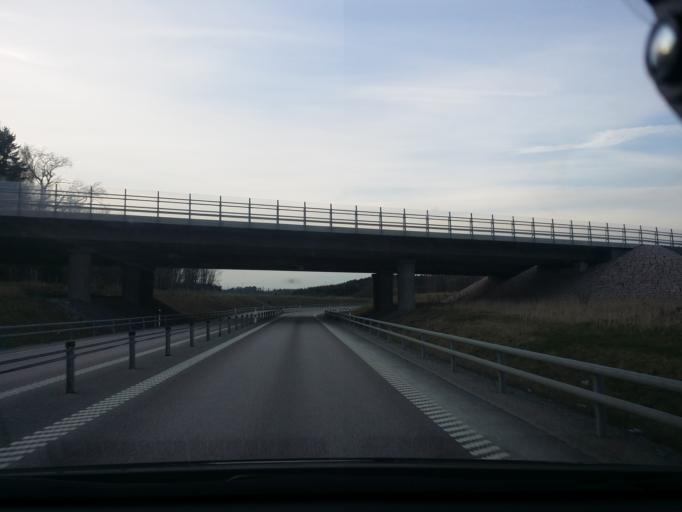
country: SE
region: Uppsala
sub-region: Enkopings Kommun
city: Enkoping
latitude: 59.6444
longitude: 17.0529
